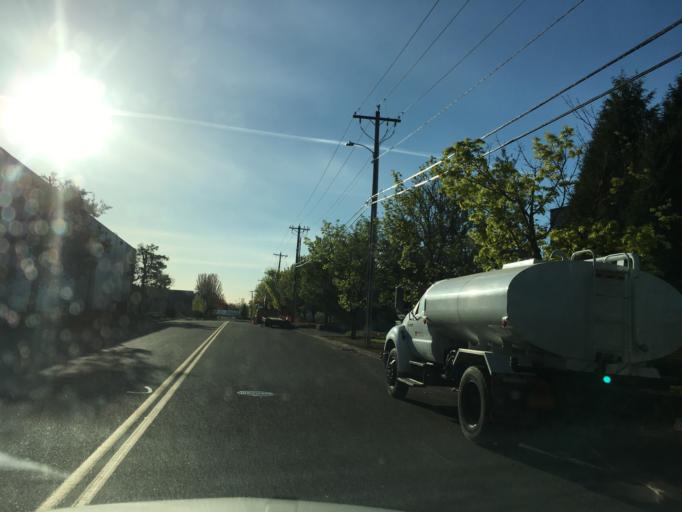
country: US
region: Oregon
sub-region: Multnomah County
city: Lents
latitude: 45.5577
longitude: -122.5251
